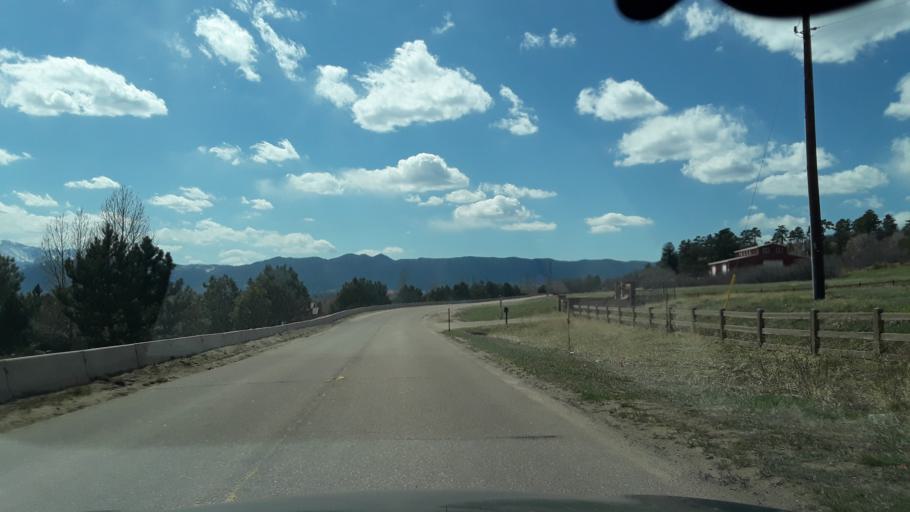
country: US
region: Colorado
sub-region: El Paso County
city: Gleneagle
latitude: 39.0349
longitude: -104.7778
